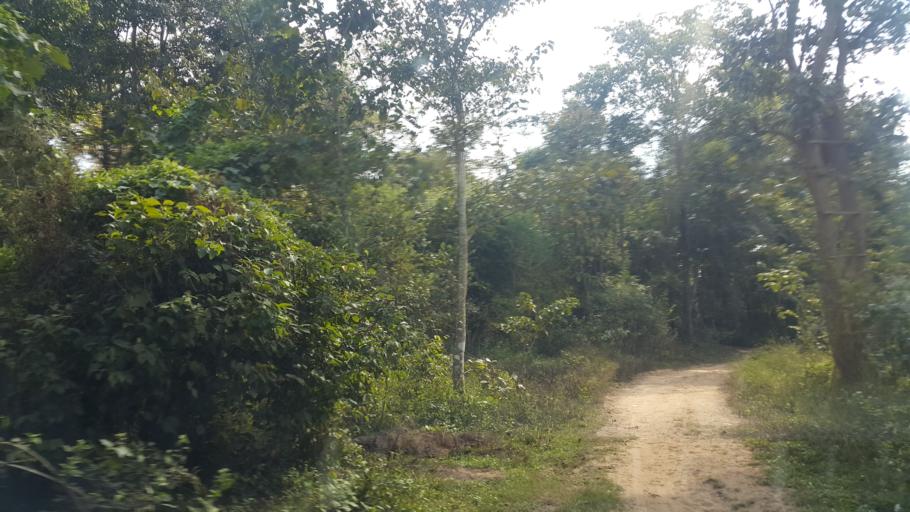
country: TH
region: Lamphun
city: Ban Thi
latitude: 18.5787
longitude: 99.1652
